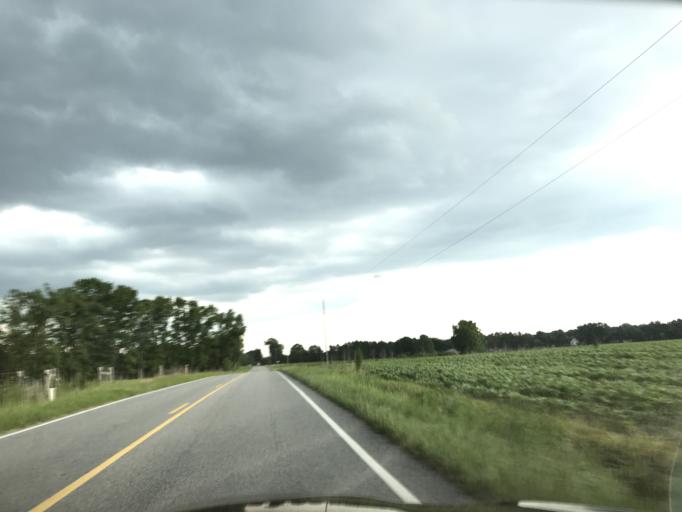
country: US
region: North Carolina
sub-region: Johnston County
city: Four Oaks
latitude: 35.5235
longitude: -78.4580
